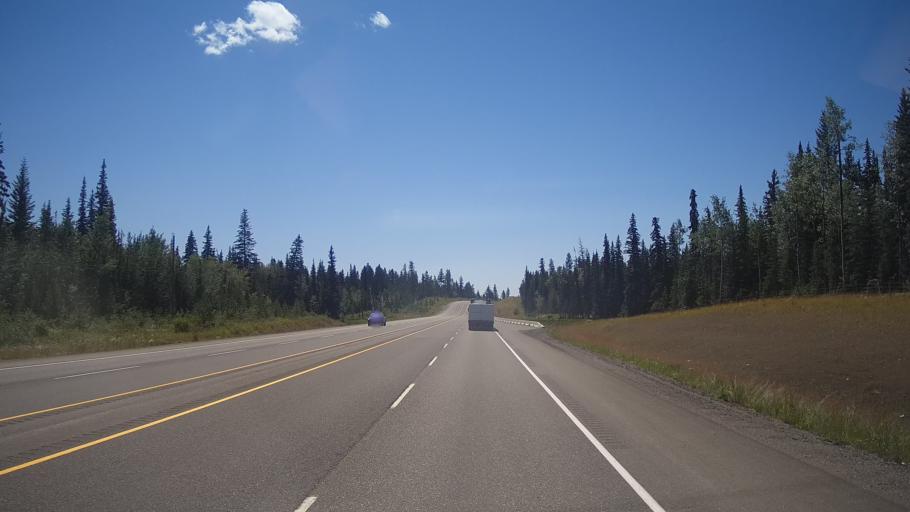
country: CA
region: British Columbia
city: Cache Creek
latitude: 51.3845
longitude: -121.3645
